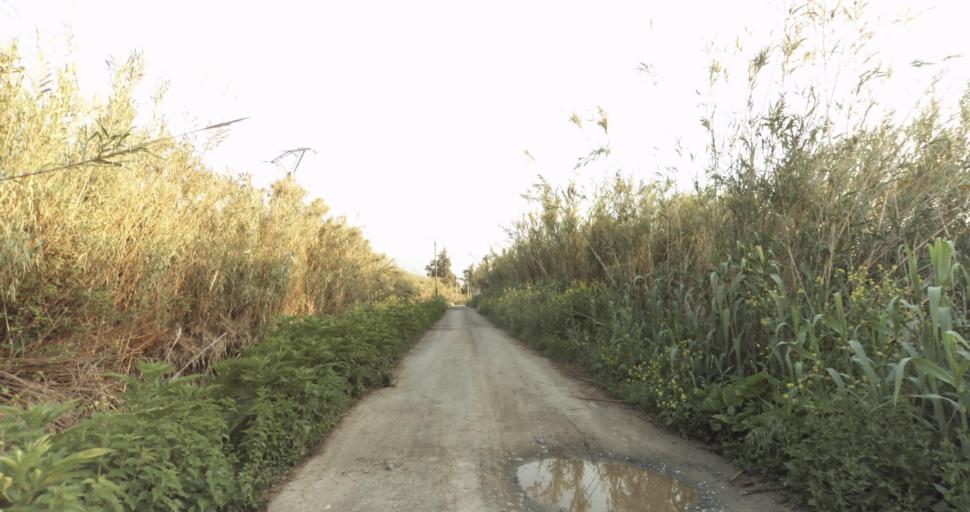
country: FR
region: Corsica
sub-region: Departement de la Haute-Corse
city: Biguglia
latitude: 42.6142
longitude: 9.4460
